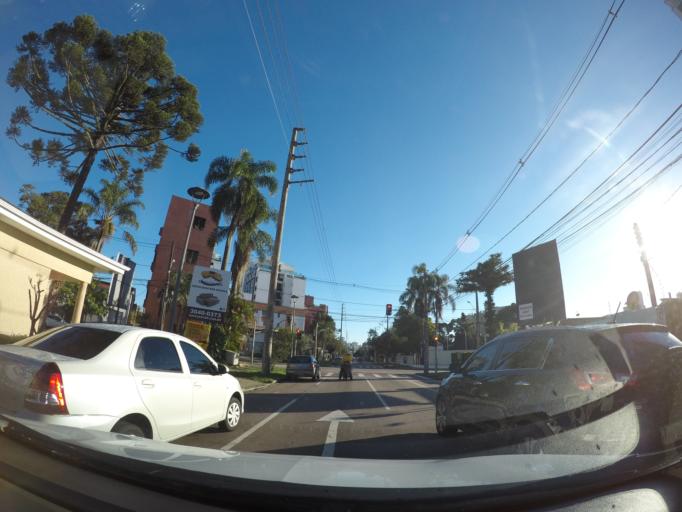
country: BR
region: Parana
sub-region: Curitiba
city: Curitiba
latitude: -25.4241
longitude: -49.2558
